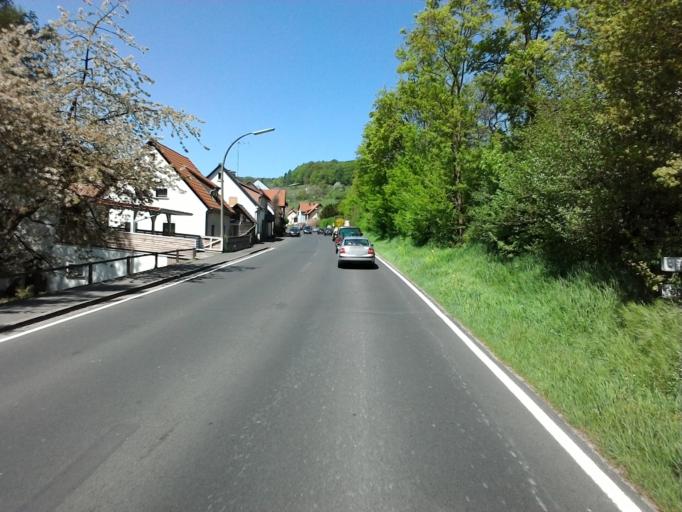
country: DE
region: Bavaria
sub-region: Regierungsbezirk Unterfranken
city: Rechtenbach
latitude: 49.9811
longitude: 9.5148
